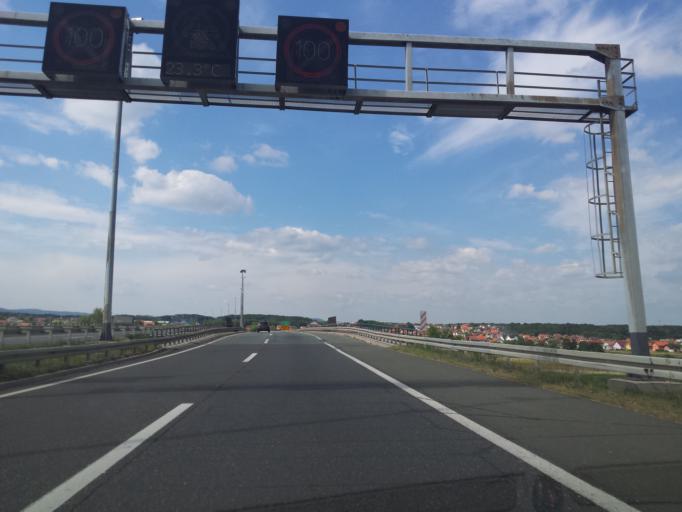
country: HR
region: Grad Zagreb
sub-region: Sesvete
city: Sesvete
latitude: 45.8175
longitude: 16.1381
